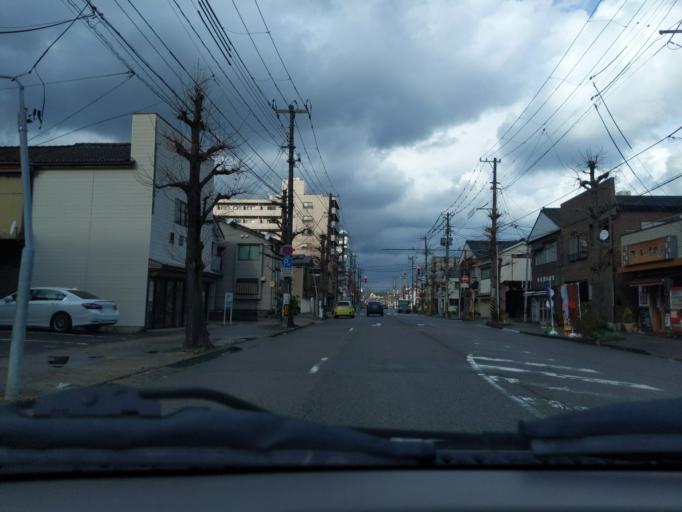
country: JP
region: Niigata
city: Niigata-shi
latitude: 37.9269
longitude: 139.0470
